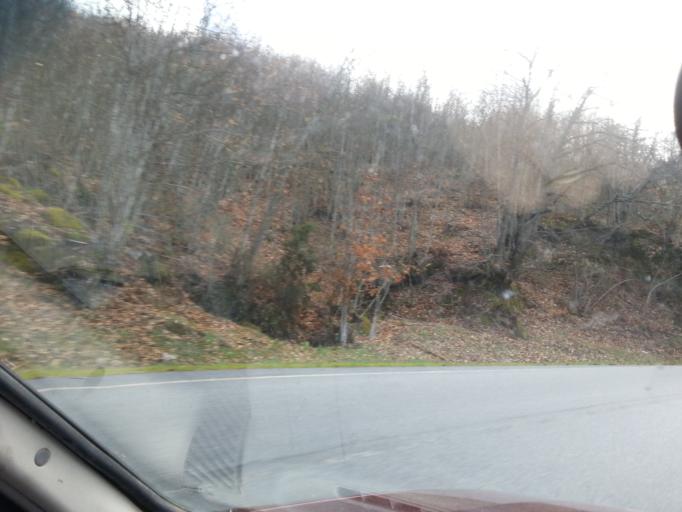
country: PT
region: Guarda
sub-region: Guarda
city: Guarda
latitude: 40.5532
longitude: -7.3073
